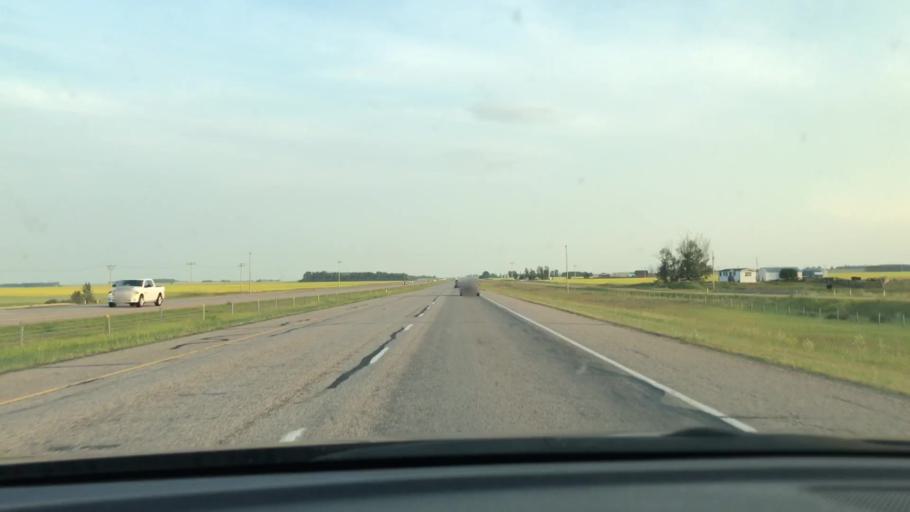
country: CA
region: Alberta
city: Olds
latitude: 51.8498
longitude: -114.0256
